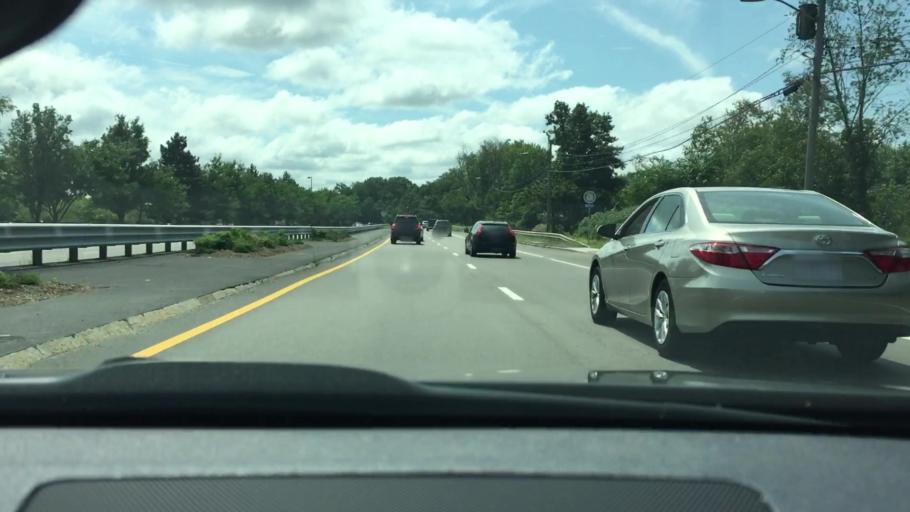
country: US
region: Massachusetts
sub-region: Norfolk County
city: Dedham
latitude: 42.2548
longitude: -71.1712
